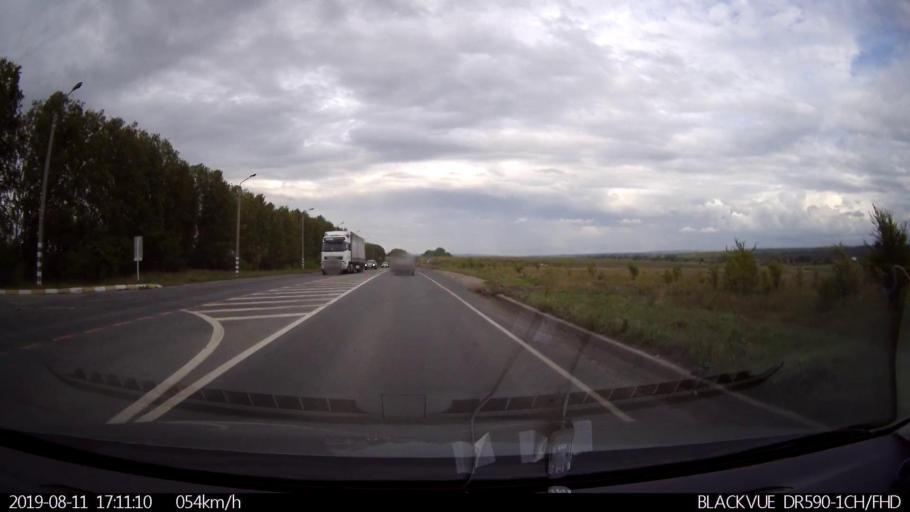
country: RU
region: Ulyanovsk
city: Mayna
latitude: 54.3001
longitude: 47.8830
